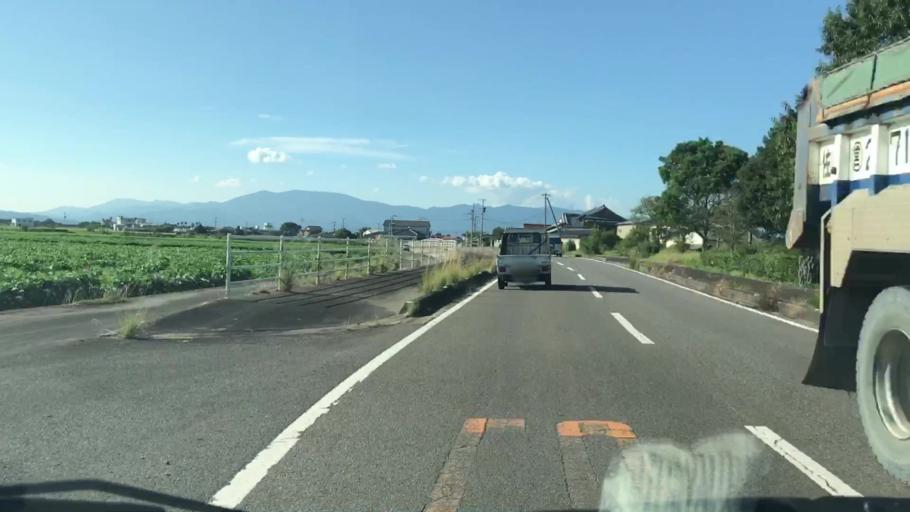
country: JP
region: Saga Prefecture
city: Saga-shi
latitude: 33.1992
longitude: 130.2670
